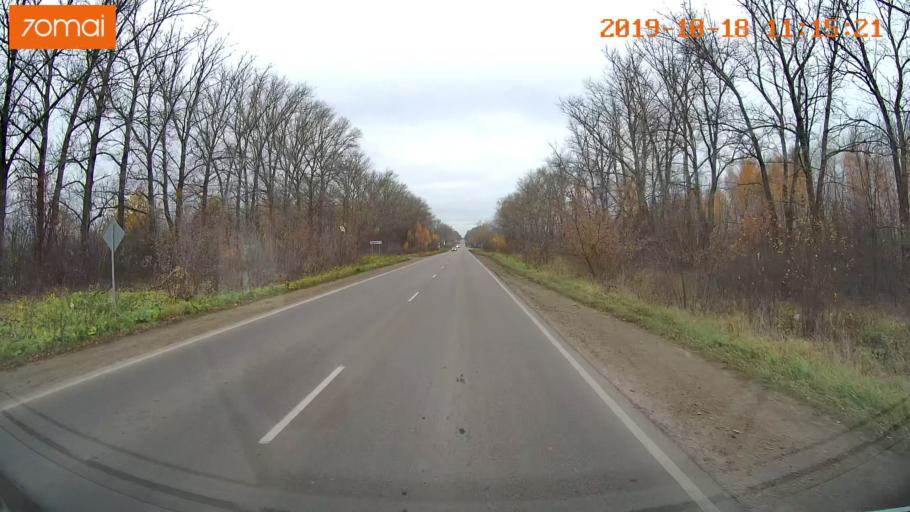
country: RU
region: Tula
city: Kimovsk
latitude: 53.9915
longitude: 38.5474
